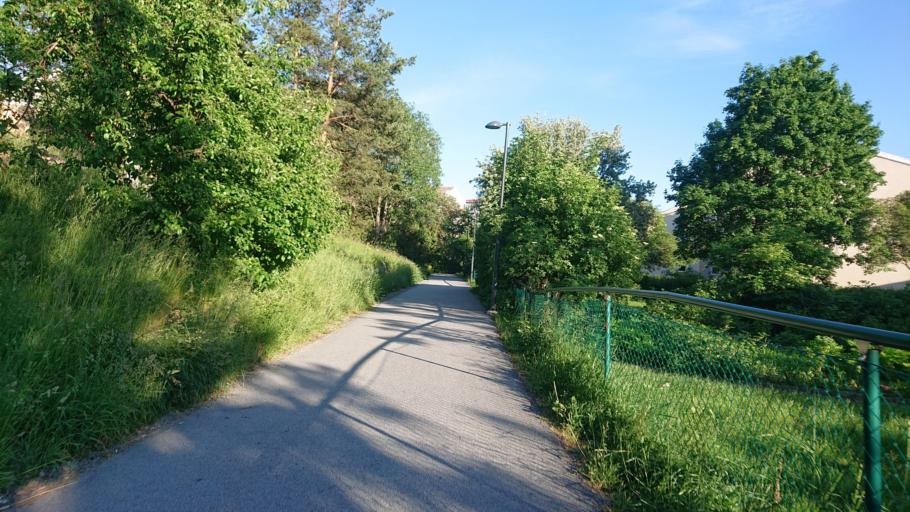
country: SE
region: Stockholm
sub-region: Osterakers Kommun
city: Akersberga
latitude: 59.4847
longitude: 18.3048
